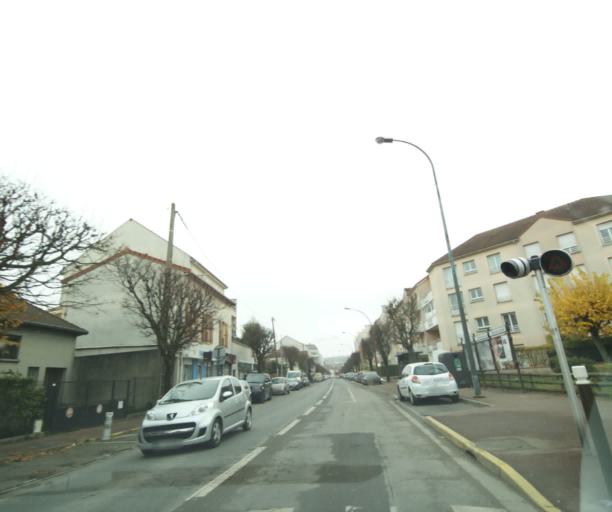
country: FR
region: Ile-de-France
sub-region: Departement de Seine-Saint-Denis
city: Livry-Gargan
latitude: 48.9293
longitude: 2.5412
